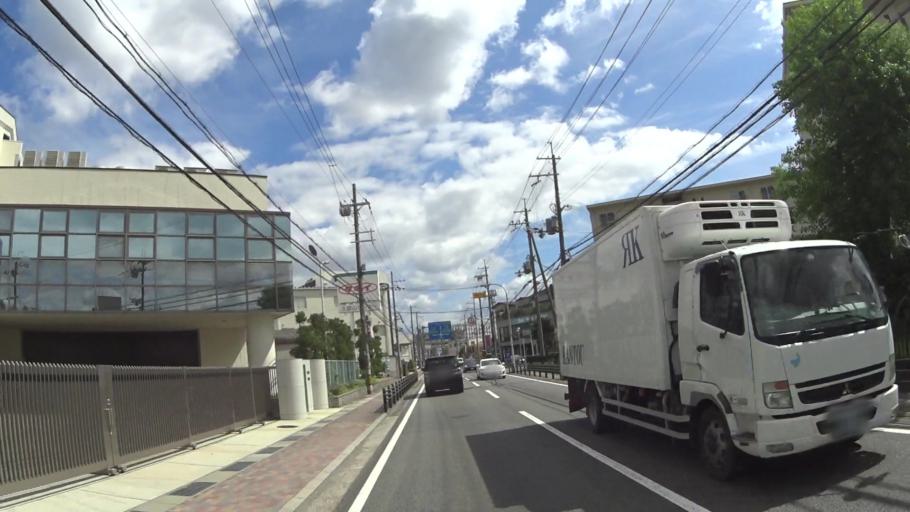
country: JP
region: Kyoto
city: Yawata
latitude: 34.8769
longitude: 135.7426
